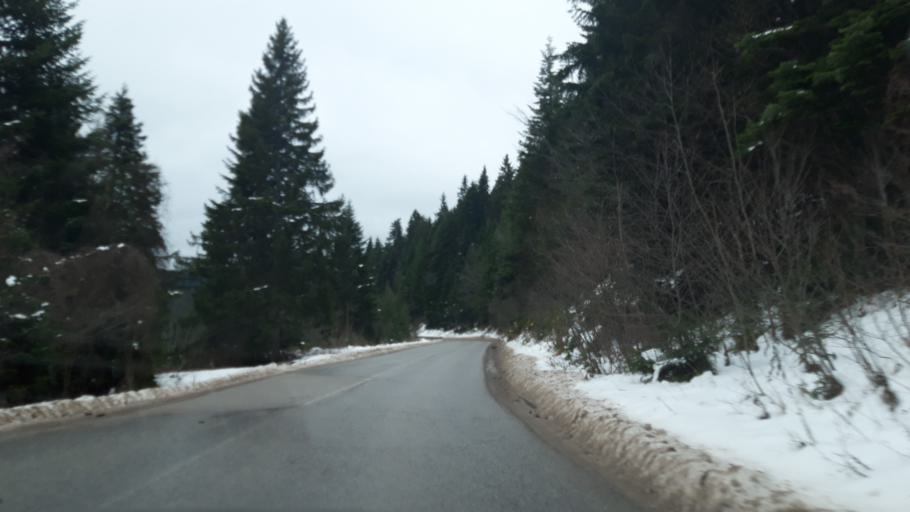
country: BA
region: Republika Srpska
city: Koran
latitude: 43.7967
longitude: 18.5555
